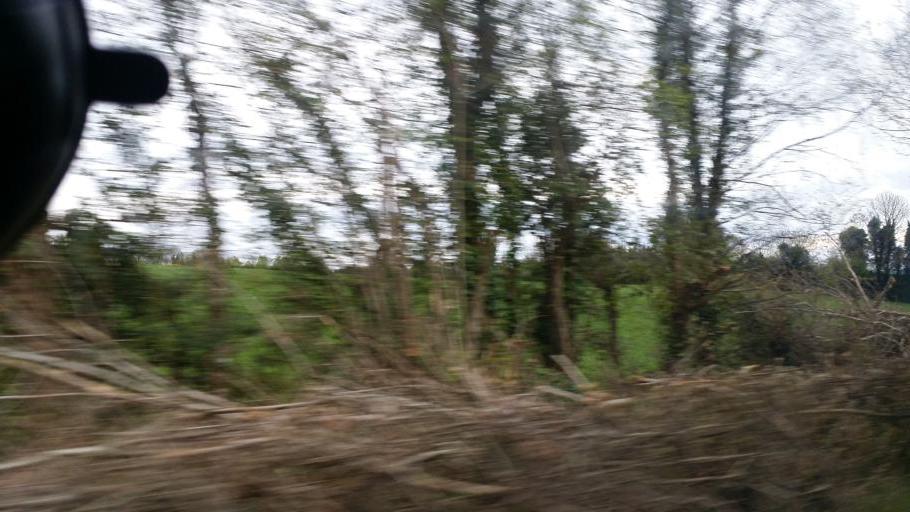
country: IE
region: Ulster
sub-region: An Cabhan
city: Ballyconnell
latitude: 54.0890
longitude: -7.5366
